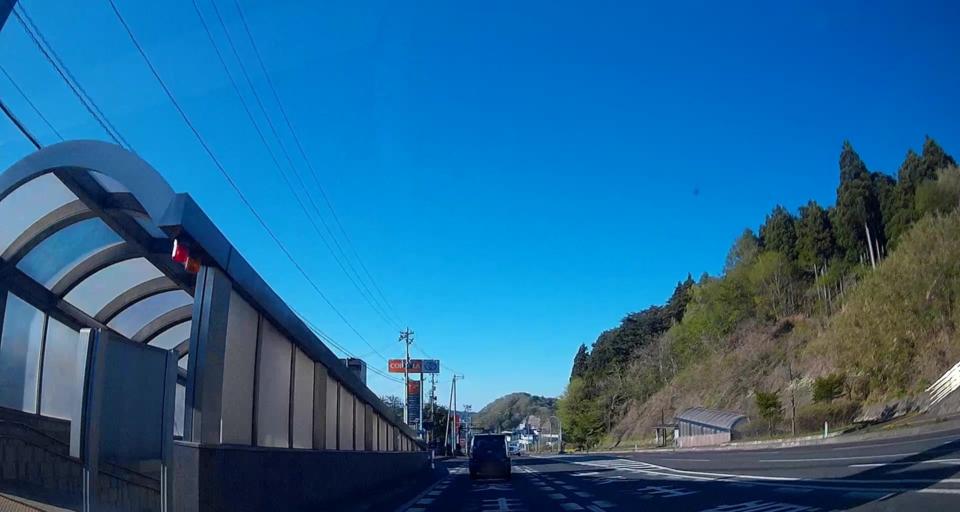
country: JP
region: Iwate
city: Miyako
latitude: 39.6178
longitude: 141.9612
